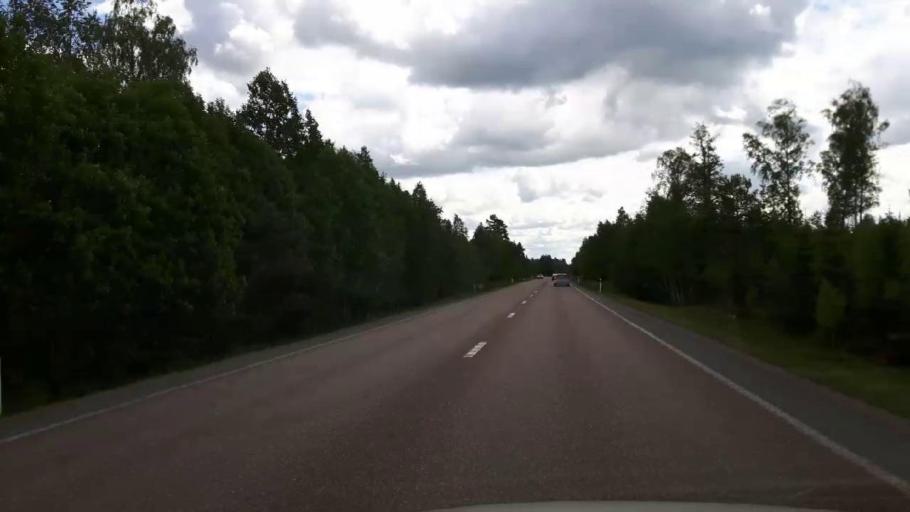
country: SE
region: Dalarna
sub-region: Saters Kommun
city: Saeter
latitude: 60.4934
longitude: 15.7607
